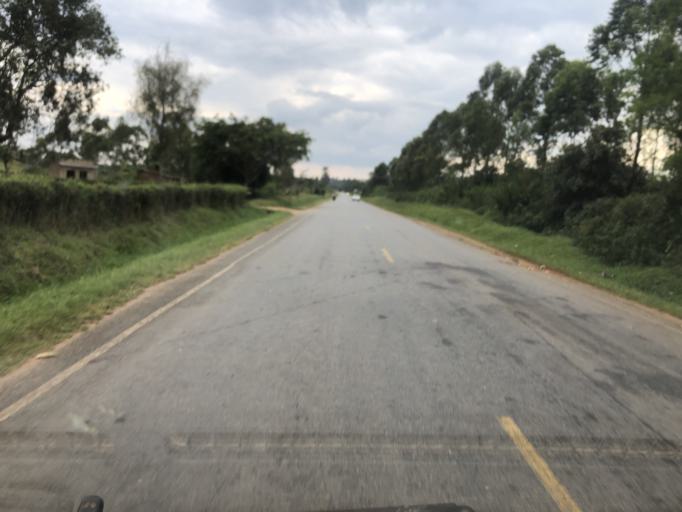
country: UG
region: Western Region
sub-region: Sheema District
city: Kibingo
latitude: -0.5797
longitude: 30.4281
